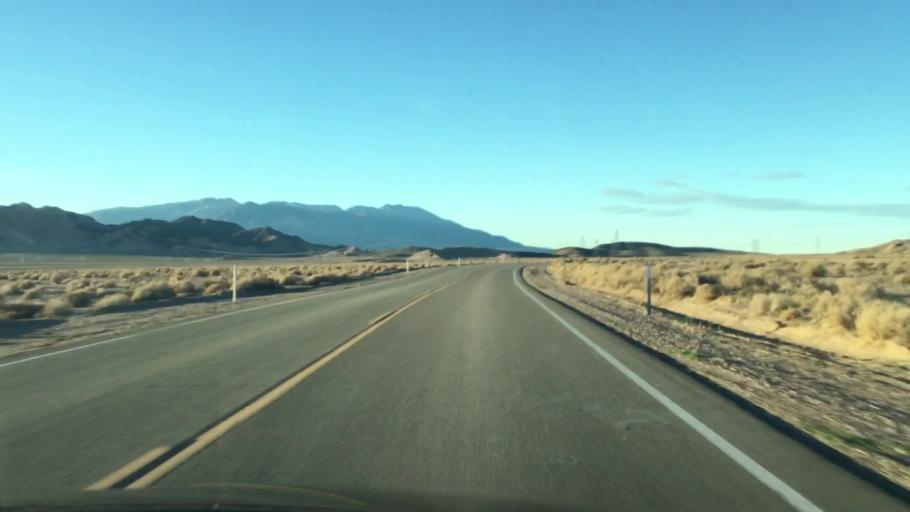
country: US
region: California
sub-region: San Bernardino County
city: Fort Irwin
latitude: 35.3740
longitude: -116.1197
